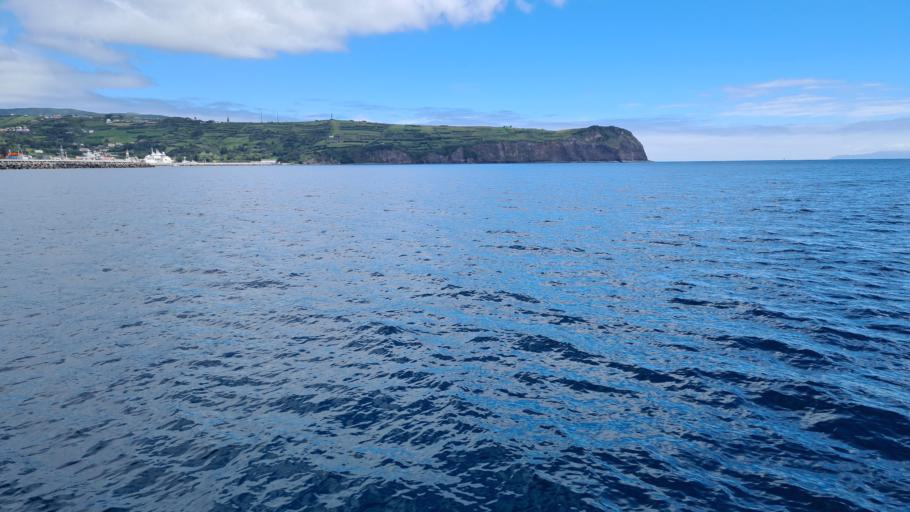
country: PT
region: Azores
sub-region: Horta
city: Horta
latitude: 38.5254
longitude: -28.6198
